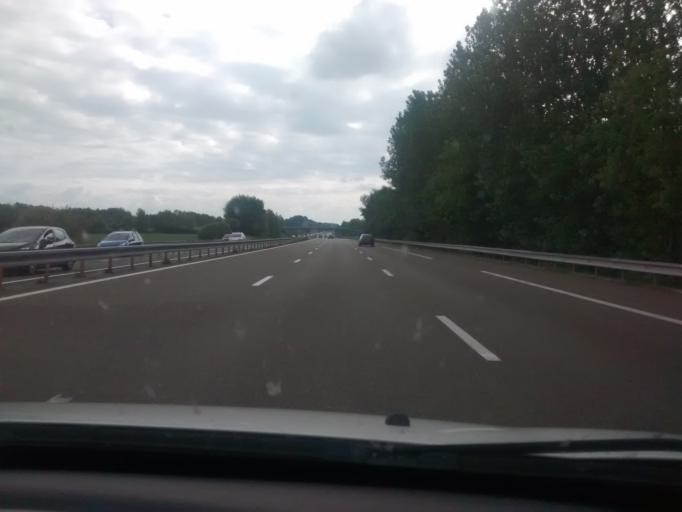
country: FR
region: Centre
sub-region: Departement d'Eure-et-Loir
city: Authon-du-Perche
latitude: 48.2225
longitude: 0.9668
